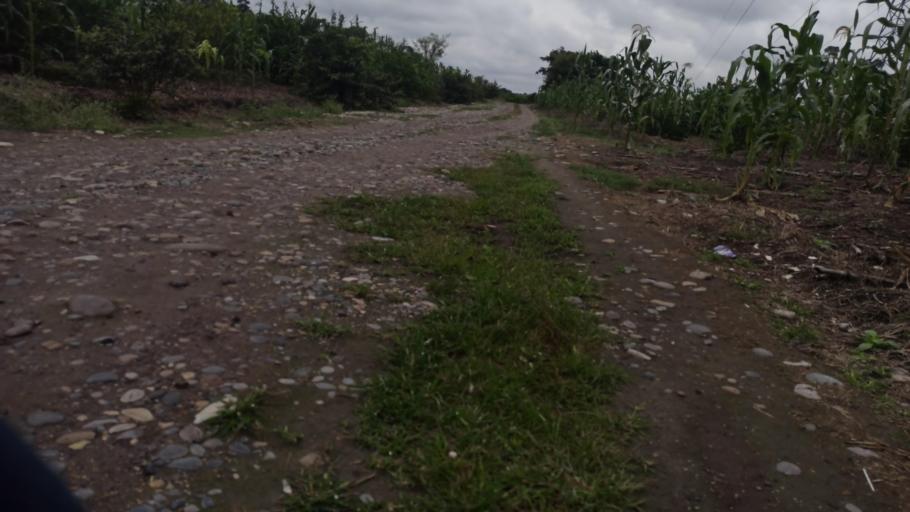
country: MX
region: Puebla
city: Espinal
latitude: 20.2970
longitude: -97.4006
